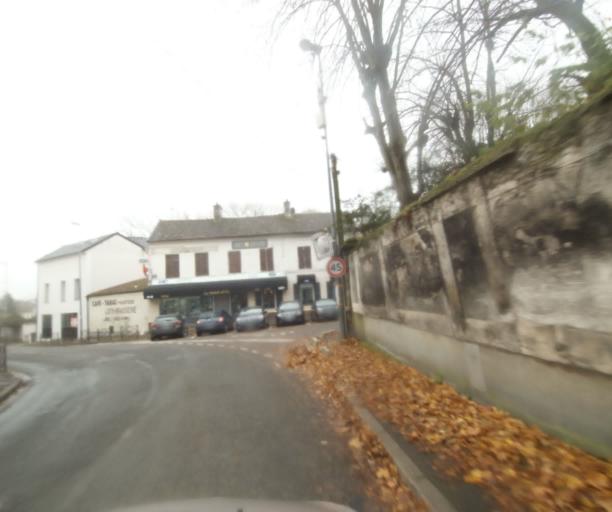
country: FR
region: Ile-de-France
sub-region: Departement de Seine-Saint-Denis
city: Coubron
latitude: 48.9153
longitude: 2.5758
